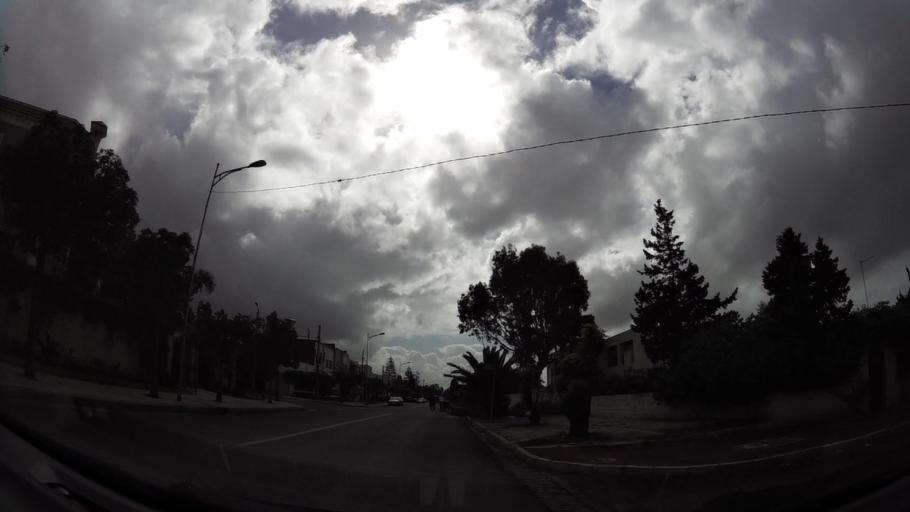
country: MA
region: Grand Casablanca
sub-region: Casablanca
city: Casablanca
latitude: 33.5541
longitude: -7.6128
